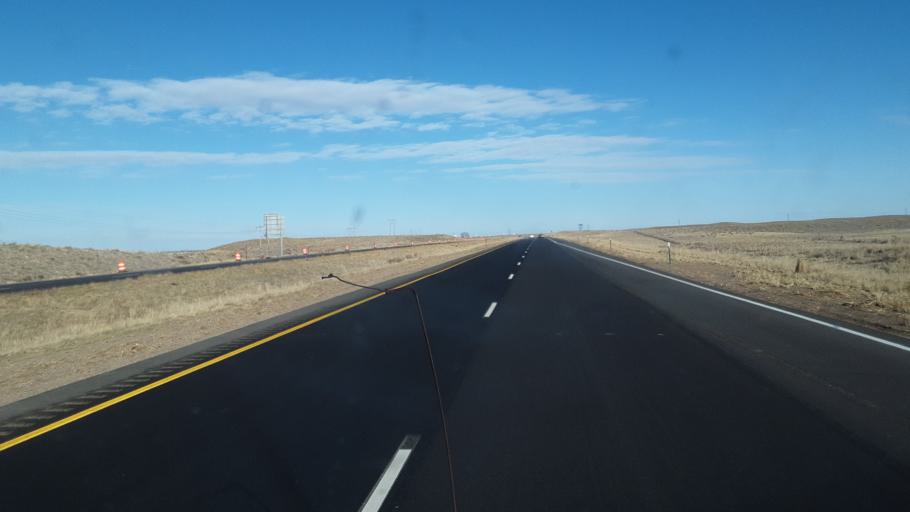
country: US
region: Colorado
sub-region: Morgan County
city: Brush
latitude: 40.2731
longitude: -103.5790
